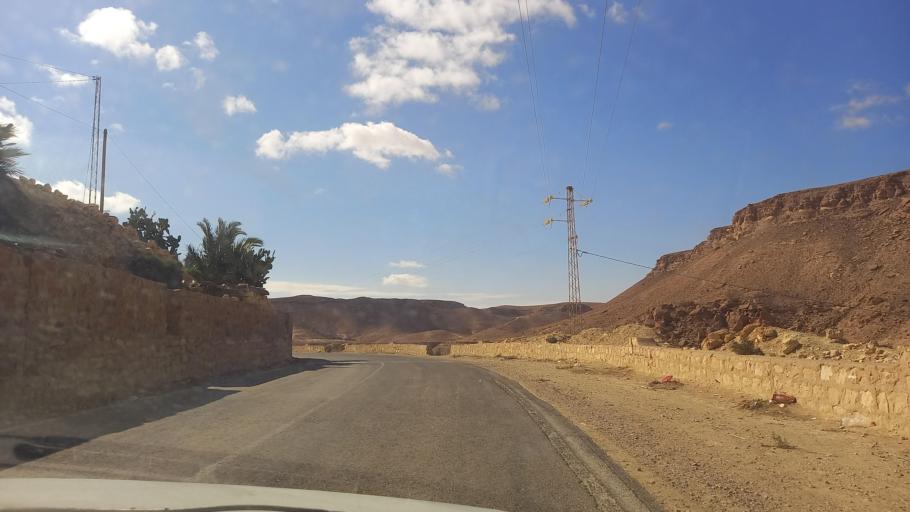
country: TN
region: Tataouine
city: Tataouine
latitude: 32.9131
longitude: 10.2592
